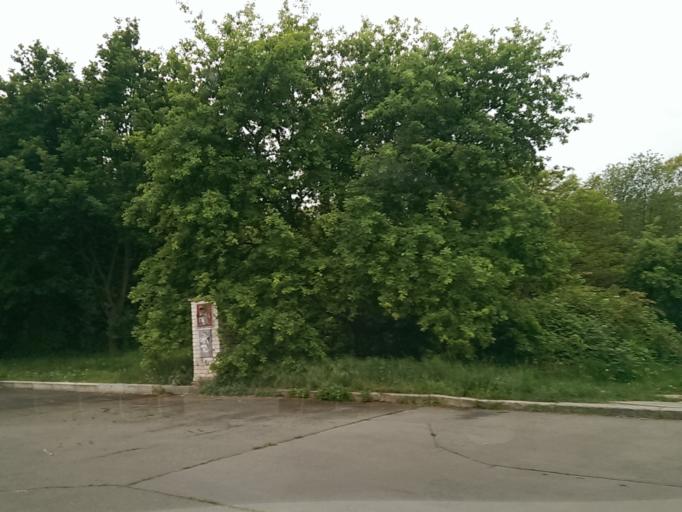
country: CZ
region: Central Bohemia
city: Vestec
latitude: 50.0377
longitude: 14.5001
